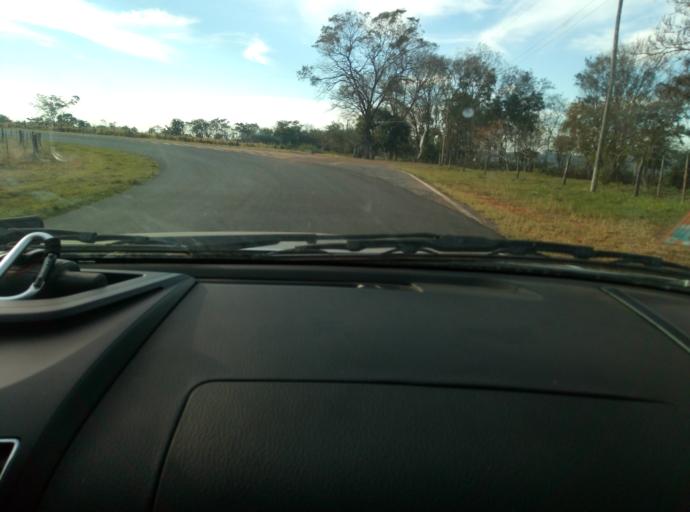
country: PY
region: Caaguazu
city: Carayao
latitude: -25.1559
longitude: -56.3116
